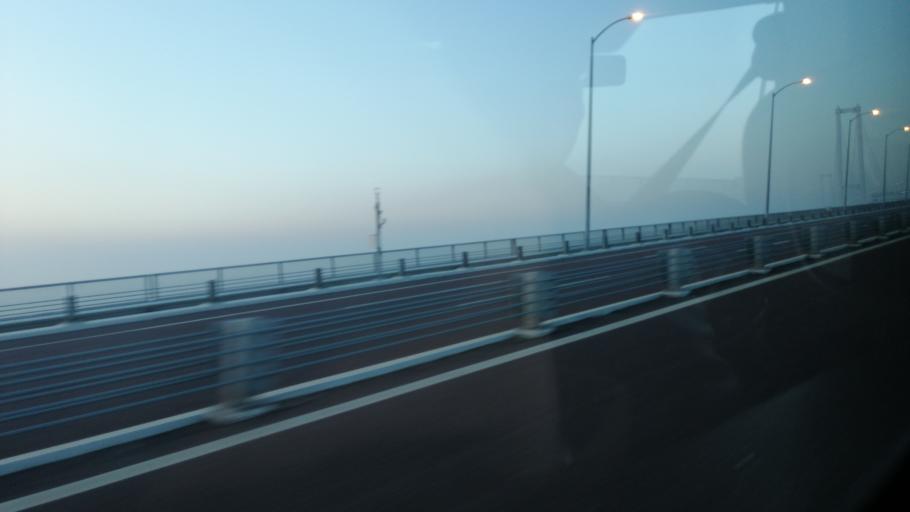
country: TR
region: Yalova
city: Altinova
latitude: 40.7352
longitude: 29.5116
